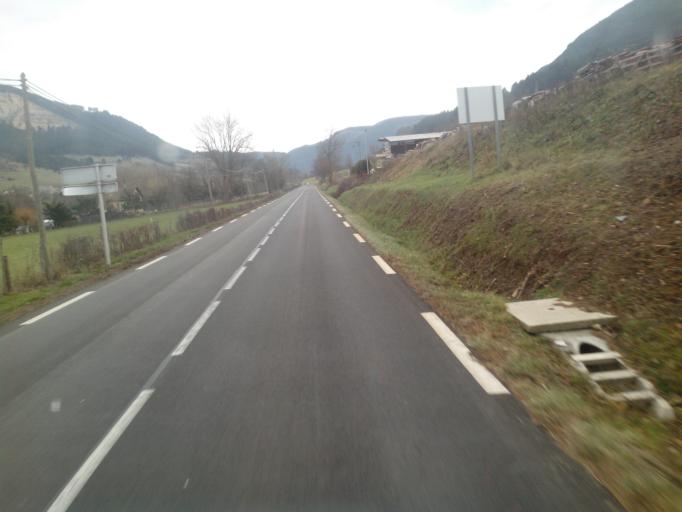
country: FR
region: Languedoc-Roussillon
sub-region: Departement de la Lozere
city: Mende
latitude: 44.4749
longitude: 3.5007
